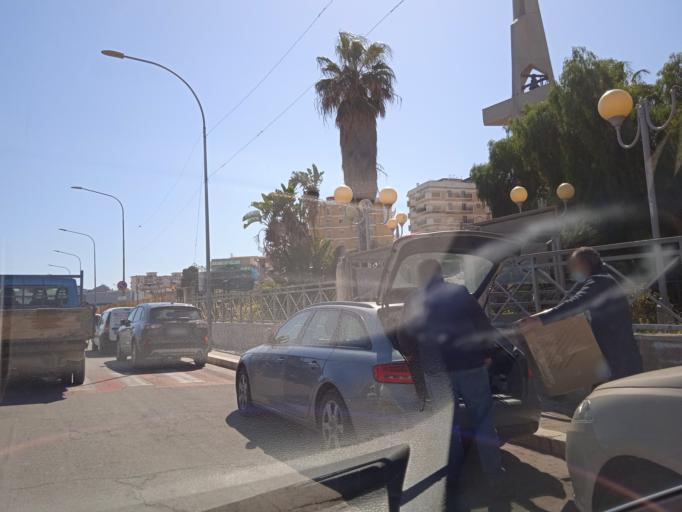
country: IT
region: Sicily
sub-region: Palermo
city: Villabate
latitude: 38.0774
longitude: 13.4486
